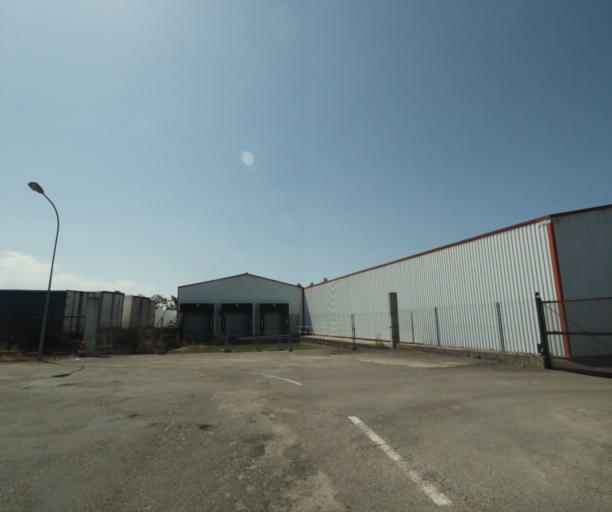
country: FR
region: Midi-Pyrenees
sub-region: Departement du Tarn-et-Garonne
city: Montauban
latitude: 44.0395
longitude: 1.3603
